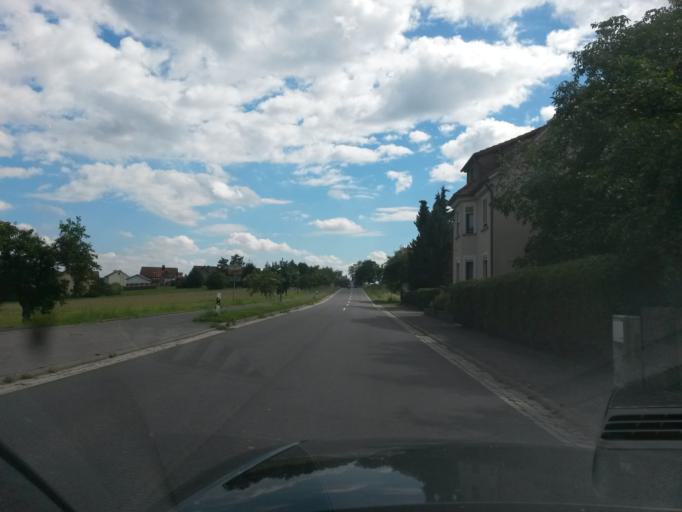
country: DE
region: Bavaria
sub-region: Regierungsbezirk Unterfranken
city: Fladungen
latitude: 50.5264
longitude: 10.1407
